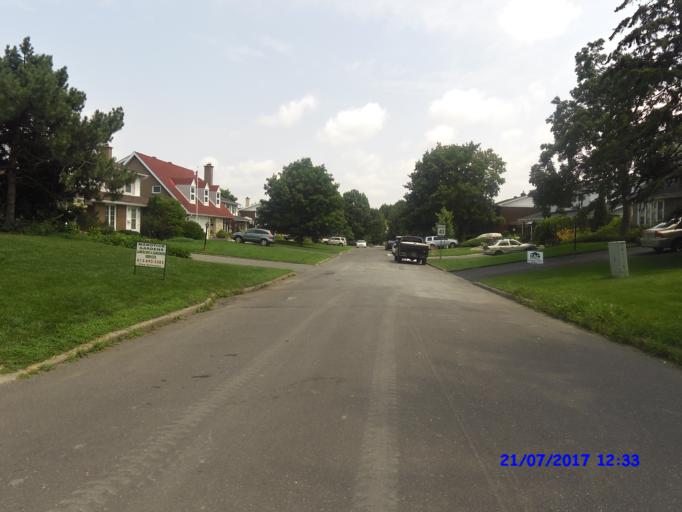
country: CA
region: Ontario
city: Ottawa
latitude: 45.3594
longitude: -75.7289
